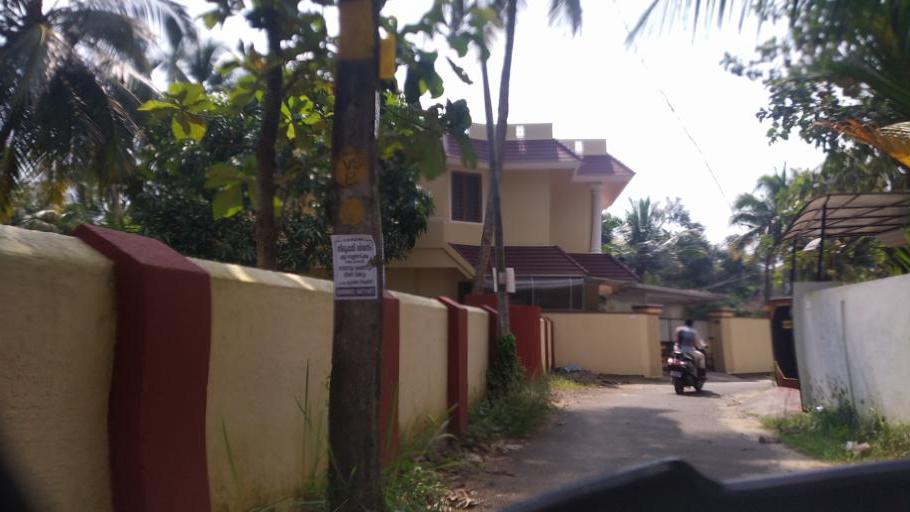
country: IN
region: Kerala
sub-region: Ernakulam
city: Elur
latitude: 10.0573
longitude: 76.2179
